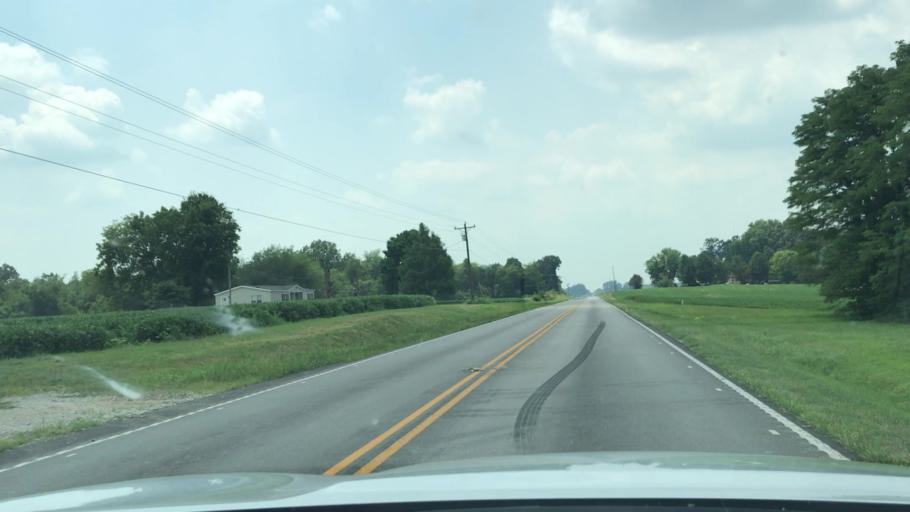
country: US
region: Kentucky
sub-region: Todd County
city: Guthrie
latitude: 36.6891
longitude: -87.1334
